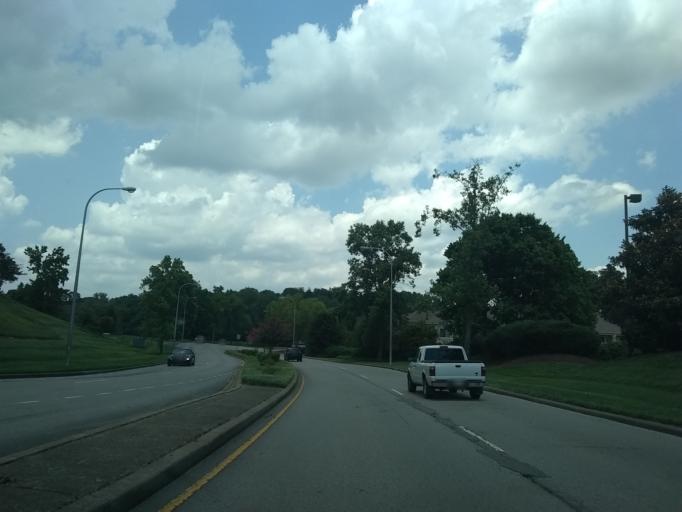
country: US
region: Tennessee
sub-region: Davidson County
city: Nashville
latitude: 36.1496
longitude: -86.6837
